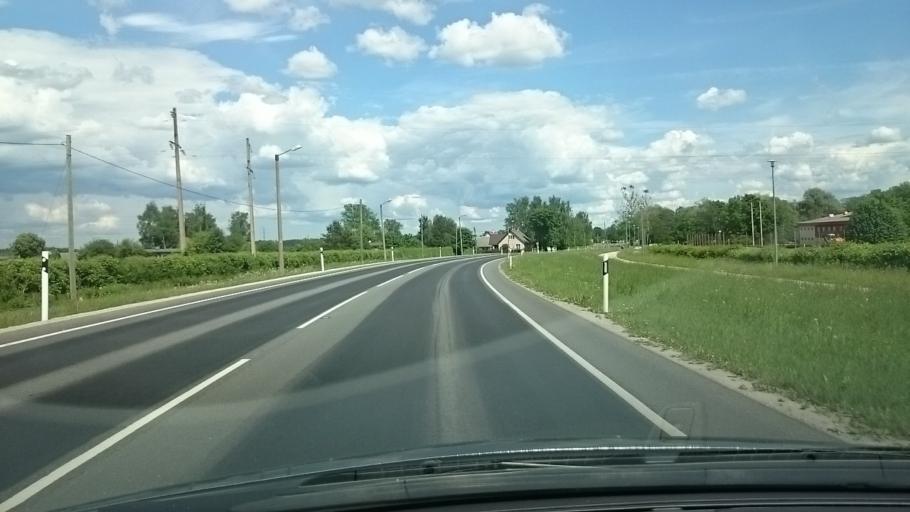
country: EE
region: Jaervamaa
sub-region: Tueri vald
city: Tueri
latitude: 58.8214
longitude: 25.4398
